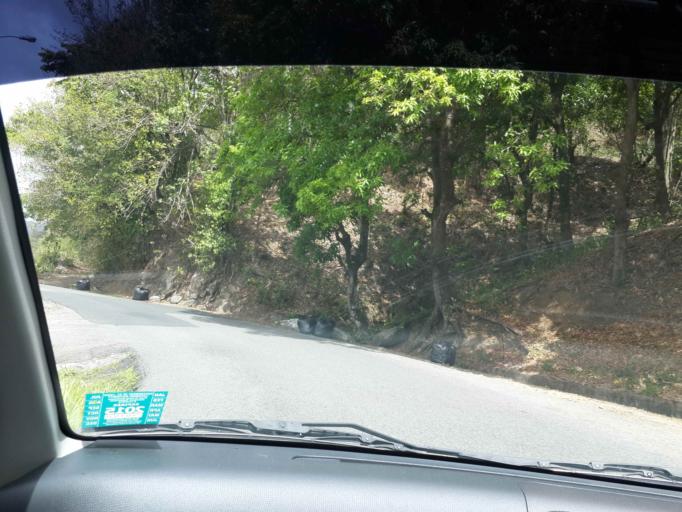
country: LC
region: Castries Quarter
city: Castries
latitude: 14.0067
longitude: -60.9967
